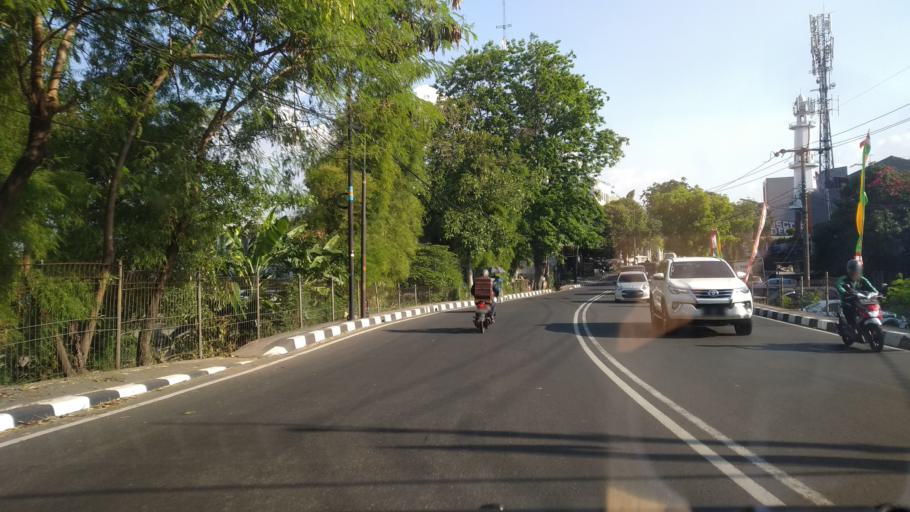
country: ID
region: Banten
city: South Tangerang
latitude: -6.2547
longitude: 106.7692
